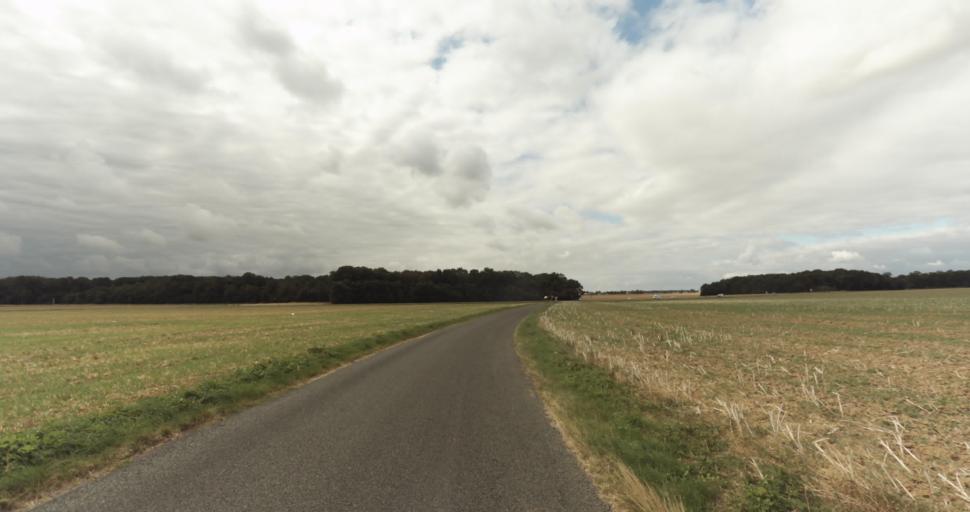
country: FR
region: Haute-Normandie
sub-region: Departement de l'Eure
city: Gravigny
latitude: 49.0155
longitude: 1.2635
